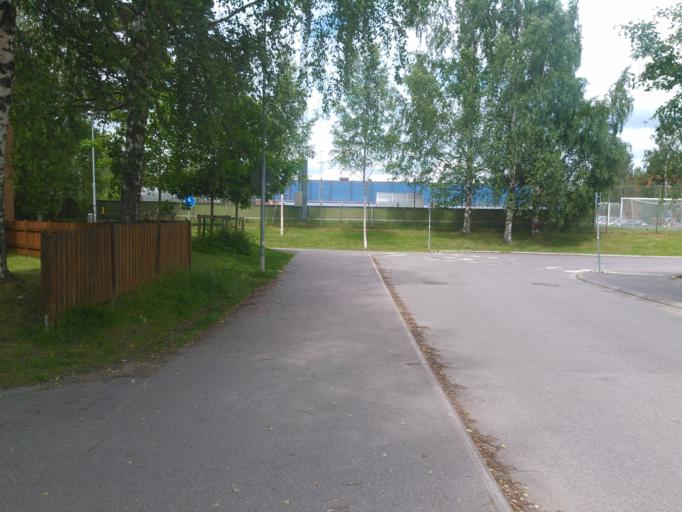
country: SE
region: Vaesterbotten
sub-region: Umea Kommun
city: Umea
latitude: 63.8091
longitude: 20.3148
